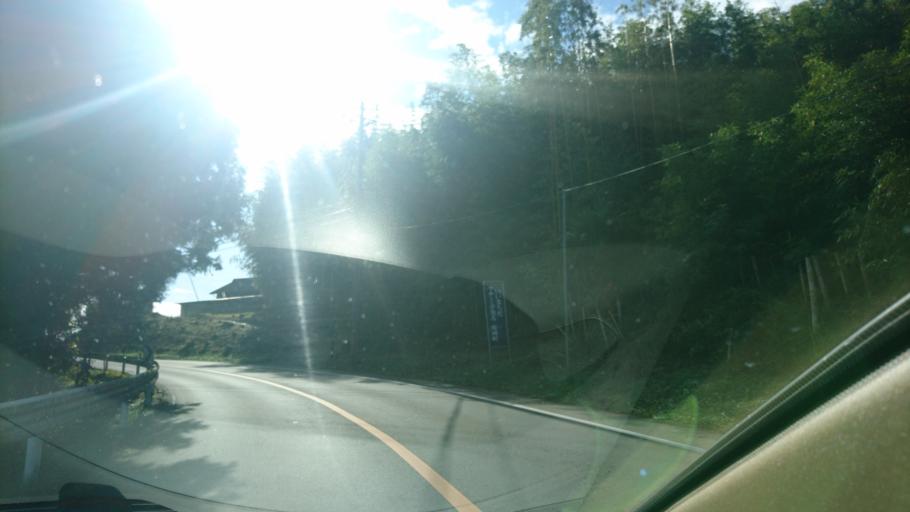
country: JP
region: Iwate
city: Ofunato
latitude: 39.0020
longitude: 141.7081
